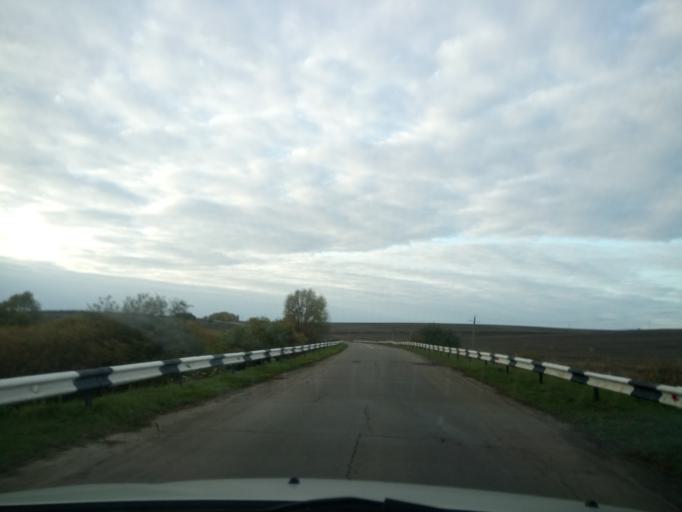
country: RU
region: Nizjnij Novgorod
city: Gagino
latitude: 55.3828
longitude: 45.0841
